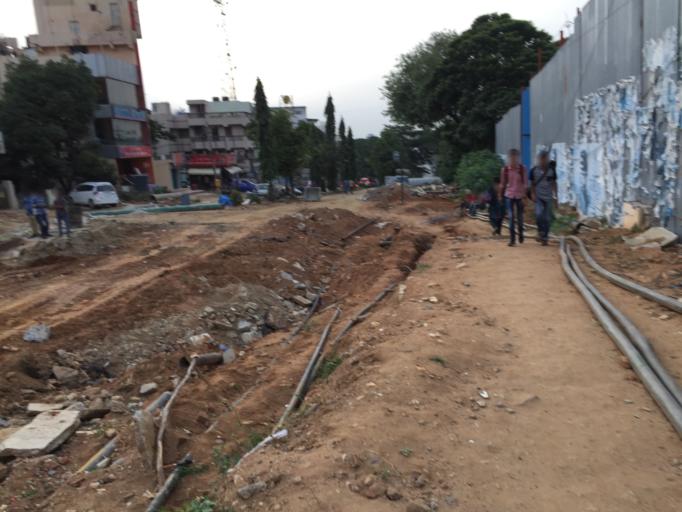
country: IN
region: Karnataka
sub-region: Bangalore Urban
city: Bangalore
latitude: 12.9312
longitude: 77.5429
